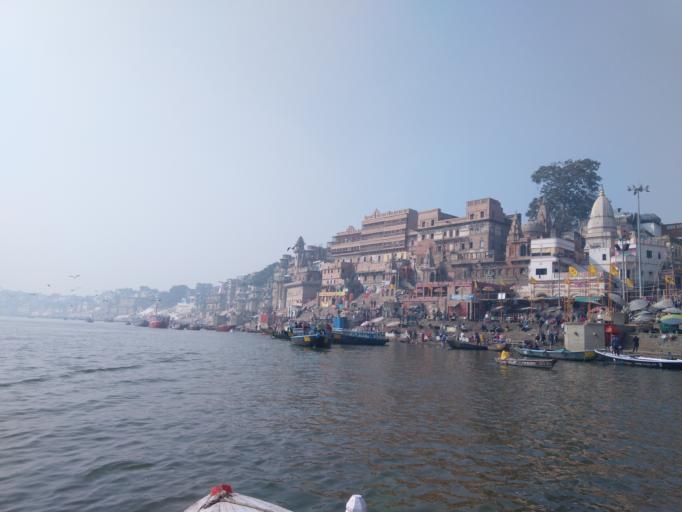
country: IN
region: Uttar Pradesh
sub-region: Varanasi
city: Varanasi
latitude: 25.3065
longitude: 83.0111
